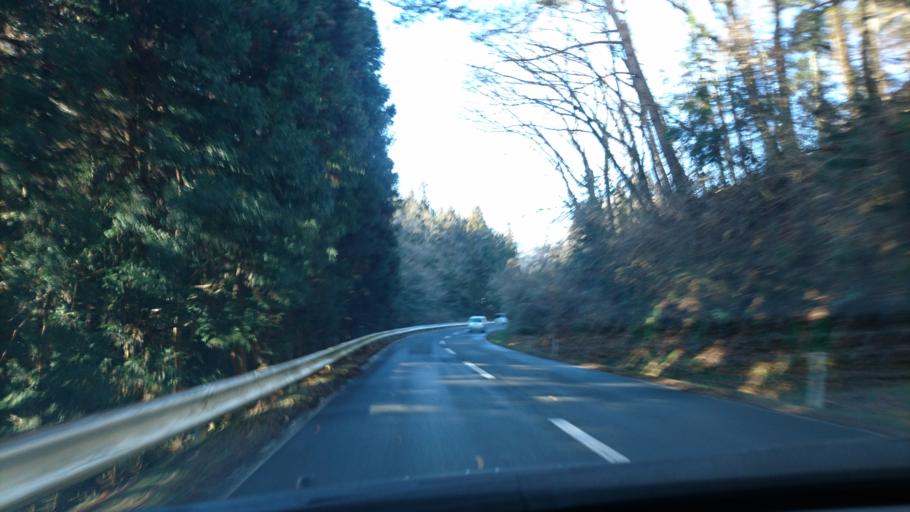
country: JP
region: Iwate
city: Ichinoseki
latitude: 38.8529
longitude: 141.2978
